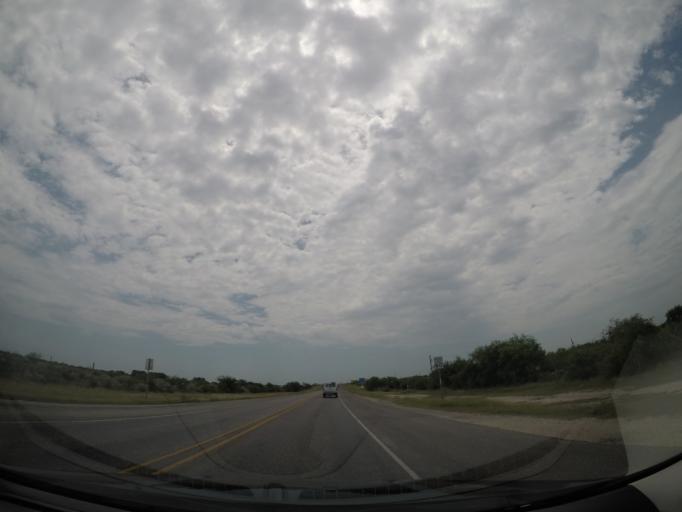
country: US
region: Texas
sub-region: Kinney County
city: Brackettville
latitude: 29.3048
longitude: -100.4063
